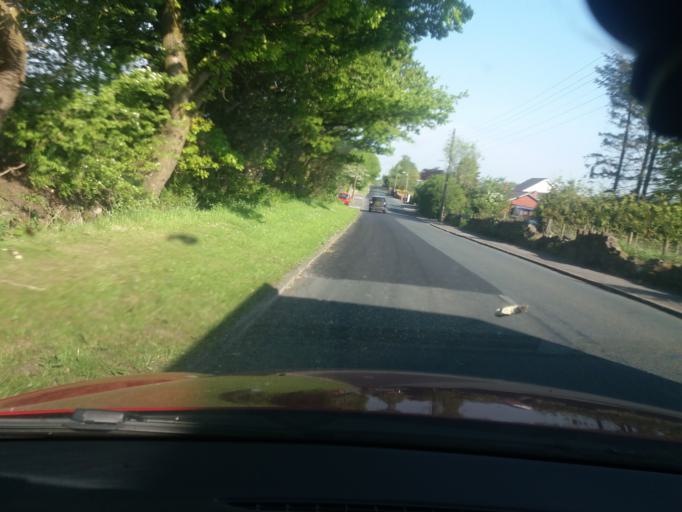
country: GB
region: England
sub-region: Lancashire
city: Adlington
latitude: 53.6287
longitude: -2.5896
